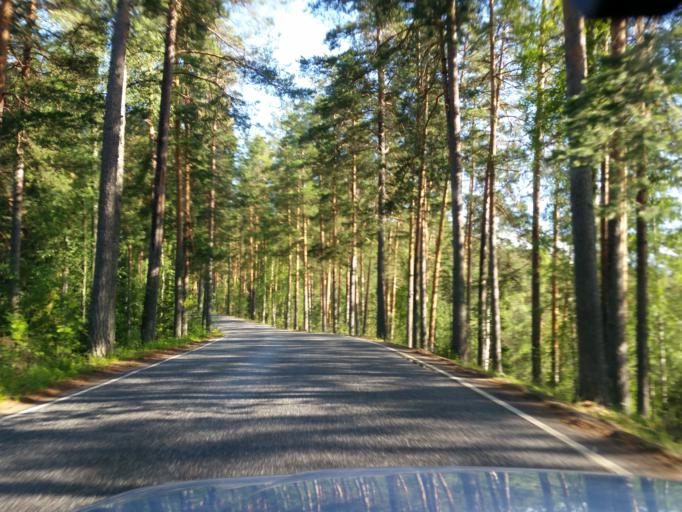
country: FI
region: Southern Savonia
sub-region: Savonlinna
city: Sulkava
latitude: 61.7946
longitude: 28.4177
